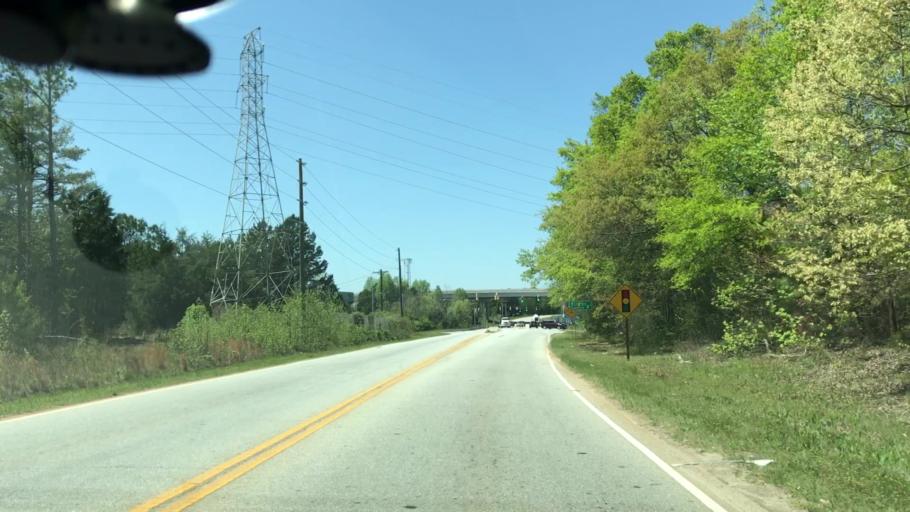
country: US
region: South Carolina
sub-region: Greenville County
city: Simpsonville
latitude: 34.7562
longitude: -82.2828
